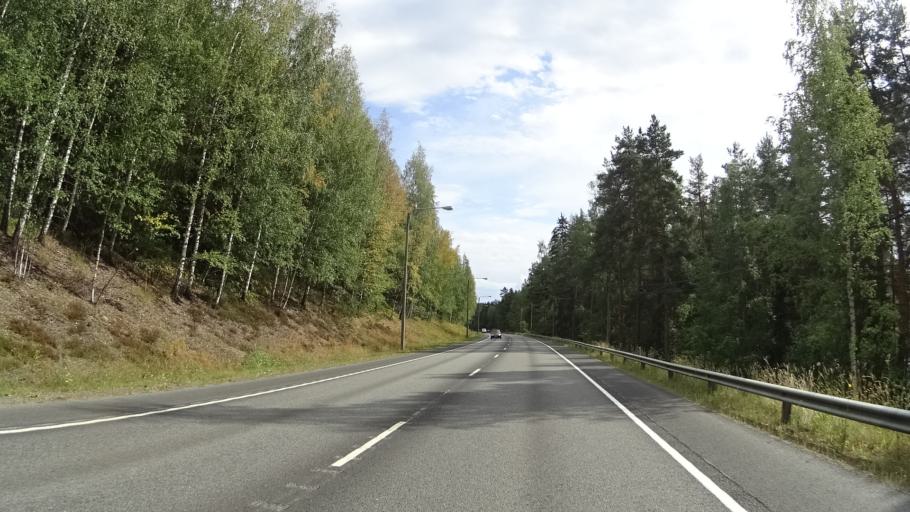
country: FI
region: Pirkanmaa
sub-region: Tampere
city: Kangasala
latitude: 61.4324
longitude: 24.1276
